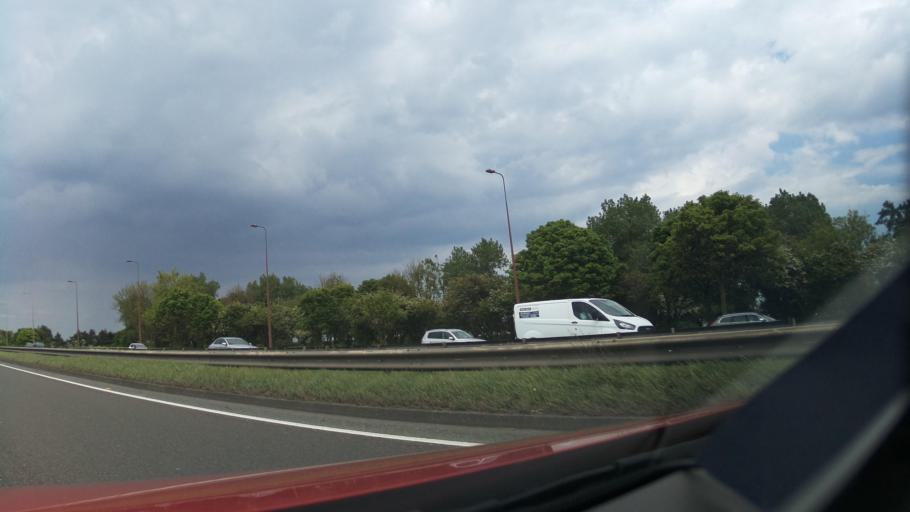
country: GB
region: England
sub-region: County Durham
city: Shotton
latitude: 54.7677
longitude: -1.3571
